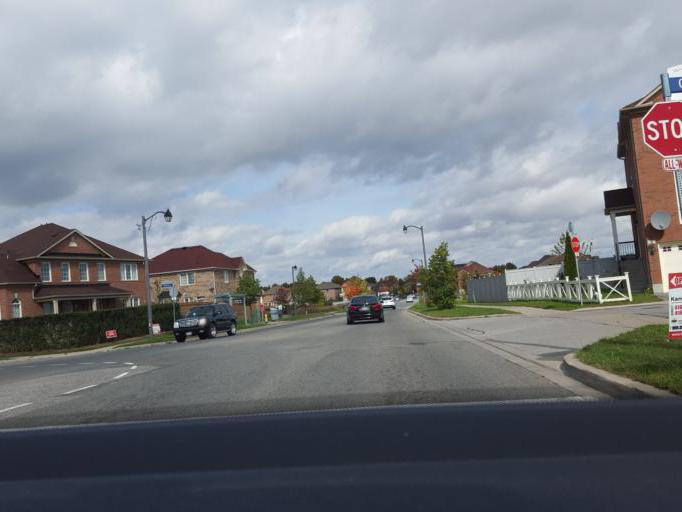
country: CA
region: Ontario
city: Scarborough
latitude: 43.8213
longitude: -79.2204
